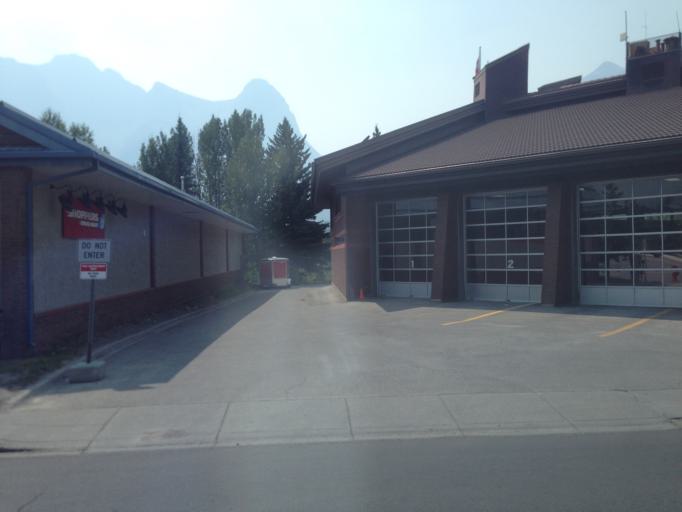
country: CA
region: Alberta
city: Canmore
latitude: 51.0907
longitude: -115.3557
